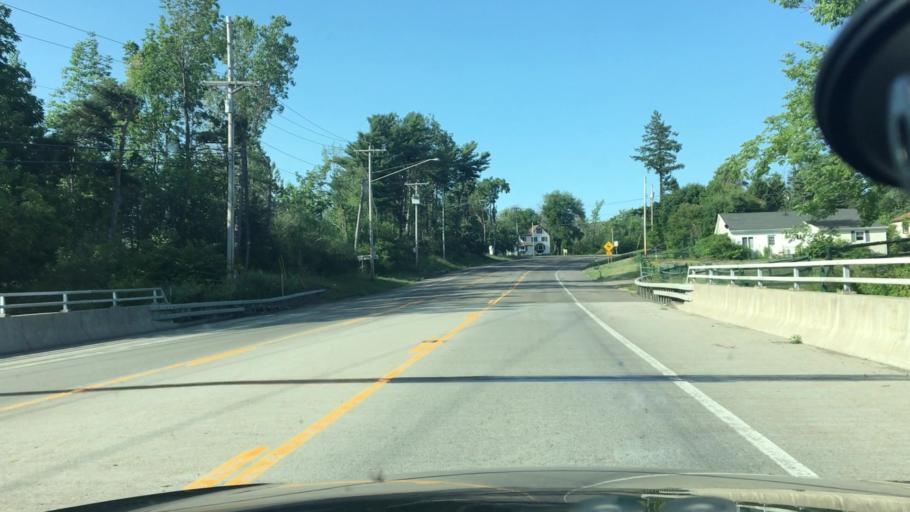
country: US
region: New York
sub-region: Erie County
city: Eden
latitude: 42.6962
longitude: -78.9359
